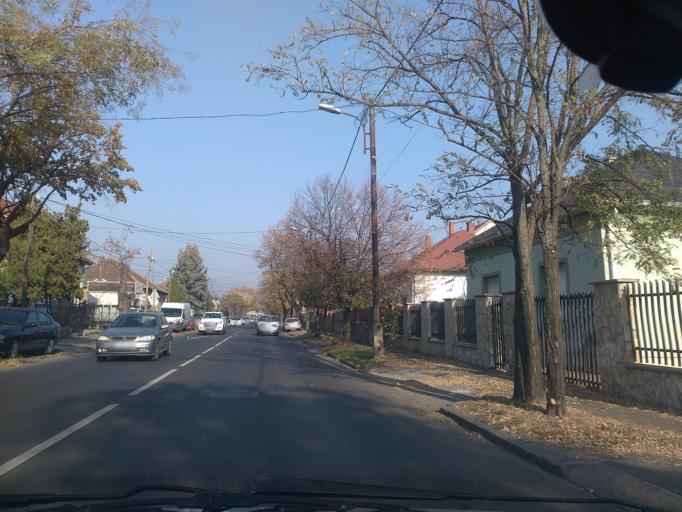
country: HU
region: Budapest
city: Budapest XVIII. keruelet
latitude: 47.4497
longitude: 19.1933
